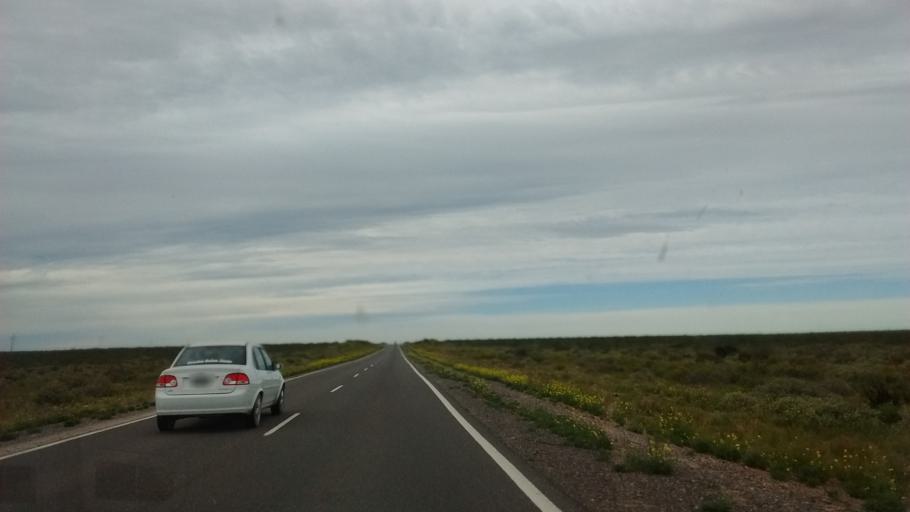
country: AR
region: Rio Negro
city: Catriel
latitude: -38.2784
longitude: -67.9947
